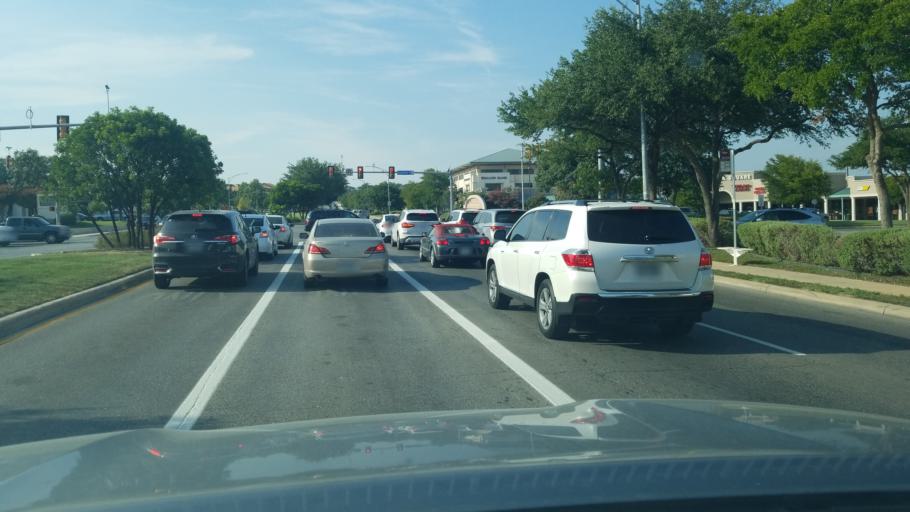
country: US
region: Texas
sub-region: Bexar County
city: Hollywood Park
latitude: 29.6263
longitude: -98.4949
